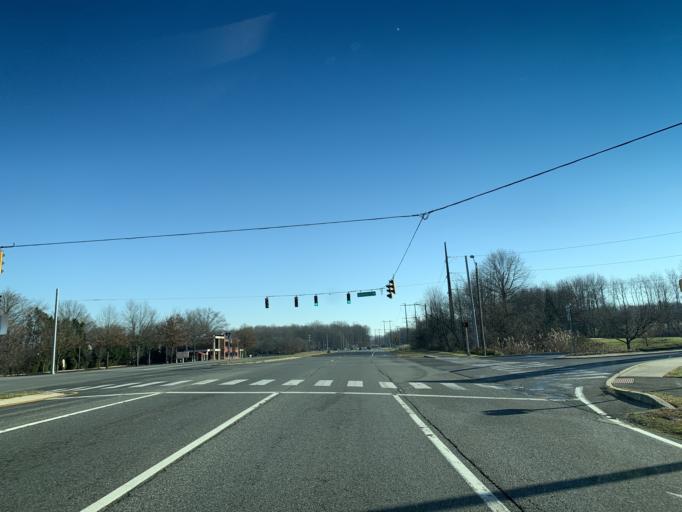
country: US
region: Delaware
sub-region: New Castle County
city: Newport
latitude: 39.6969
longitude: -75.6568
